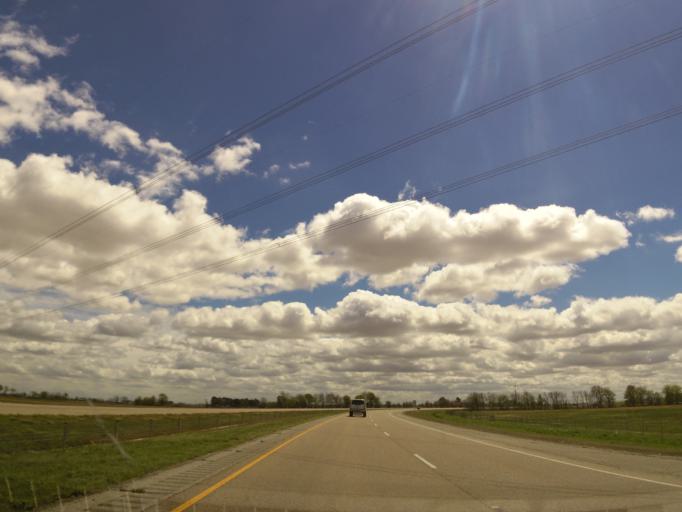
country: US
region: Arkansas
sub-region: Craighead County
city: Bay
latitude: 35.7702
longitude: -90.5791
